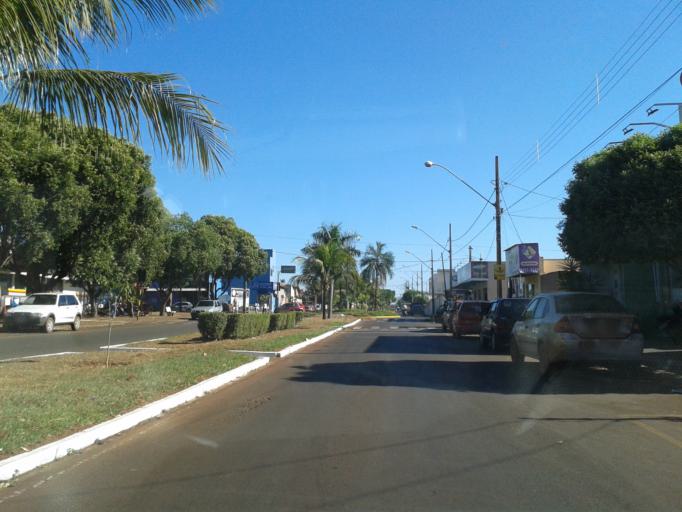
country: BR
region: Minas Gerais
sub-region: Santa Vitoria
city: Santa Vitoria
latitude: -18.8468
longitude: -50.1234
